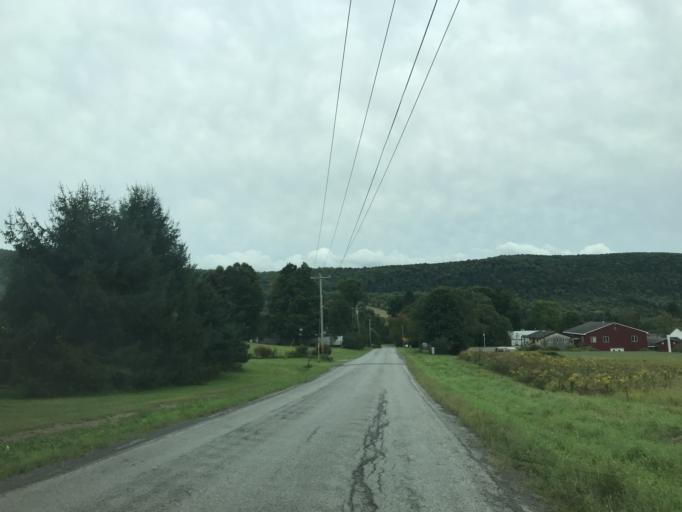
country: US
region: New York
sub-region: Otsego County
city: Worcester
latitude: 42.5480
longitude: -74.6651
